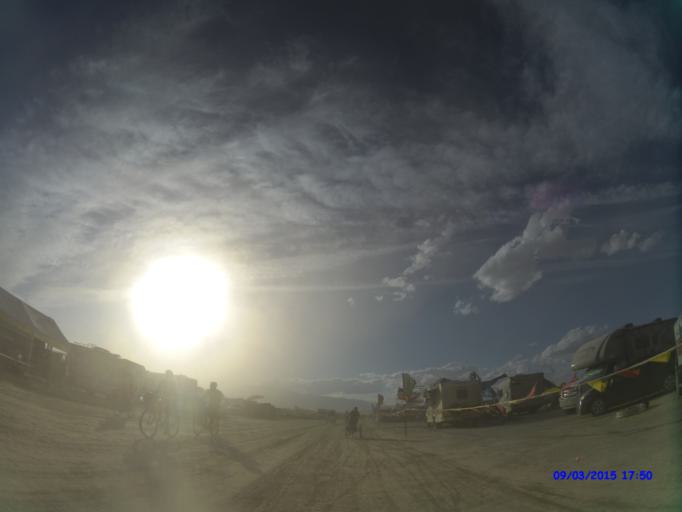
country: US
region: Nevada
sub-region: Pershing County
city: Lovelock
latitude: 40.7755
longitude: -119.2131
